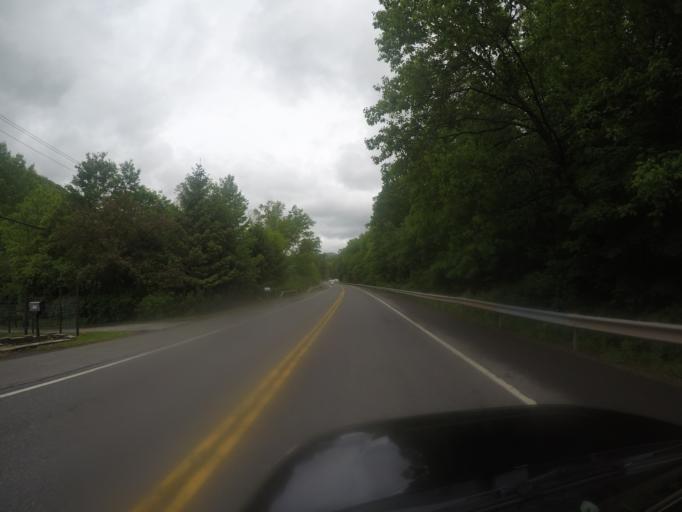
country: US
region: New York
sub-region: Ulster County
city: Shokan
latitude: 42.1137
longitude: -74.3605
